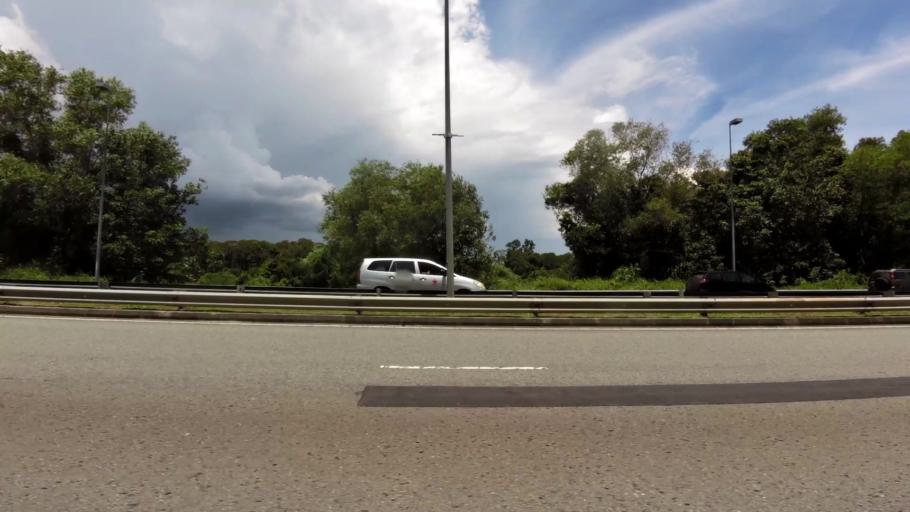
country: BN
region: Brunei and Muara
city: Bandar Seri Begawan
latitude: 4.9519
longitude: 114.9032
